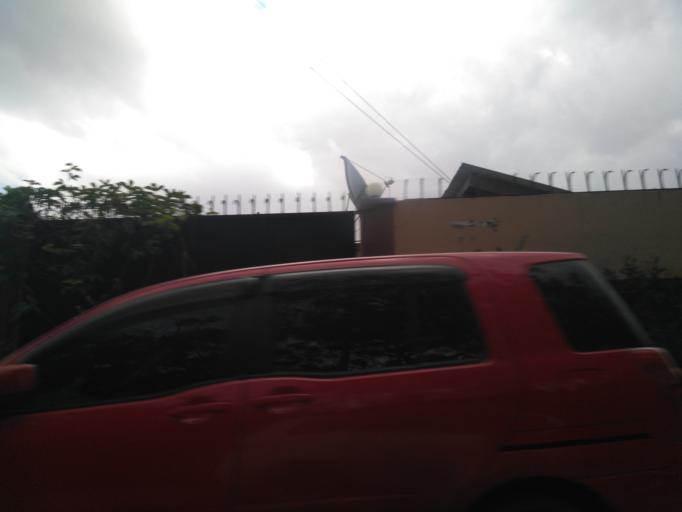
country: TZ
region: Dar es Salaam
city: Magomeni
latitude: -6.7953
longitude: 39.2717
